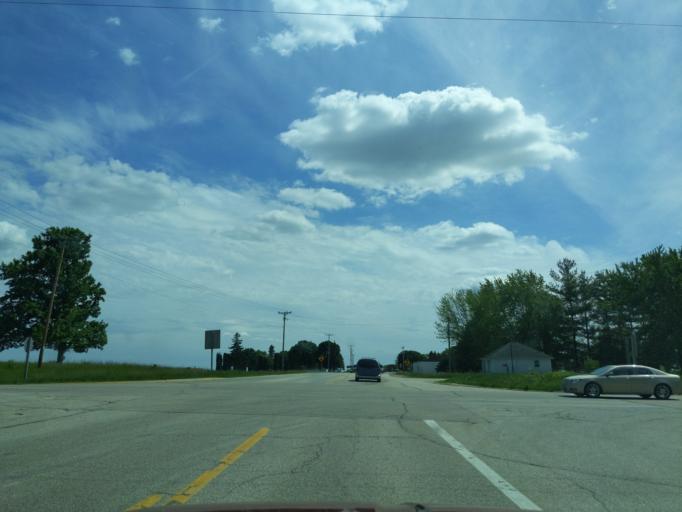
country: US
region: Wisconsin
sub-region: Dane County
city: De Forest
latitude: 43.3323
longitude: -89.3253
